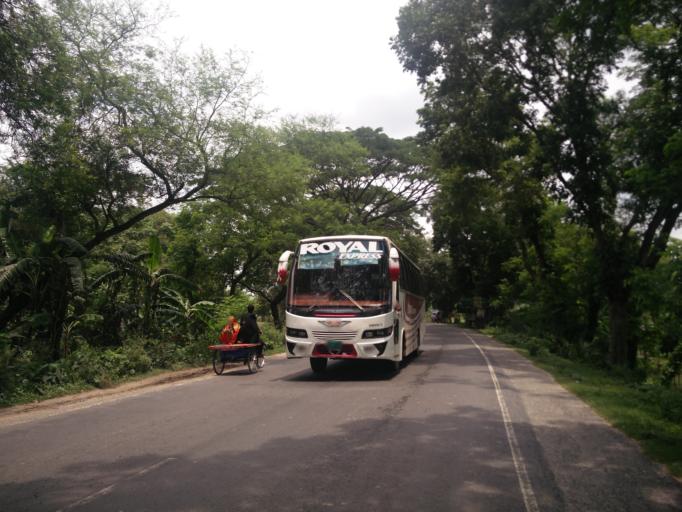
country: BD
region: Khulna
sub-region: Magura
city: Magura
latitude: 23.5435
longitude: 89.5339
